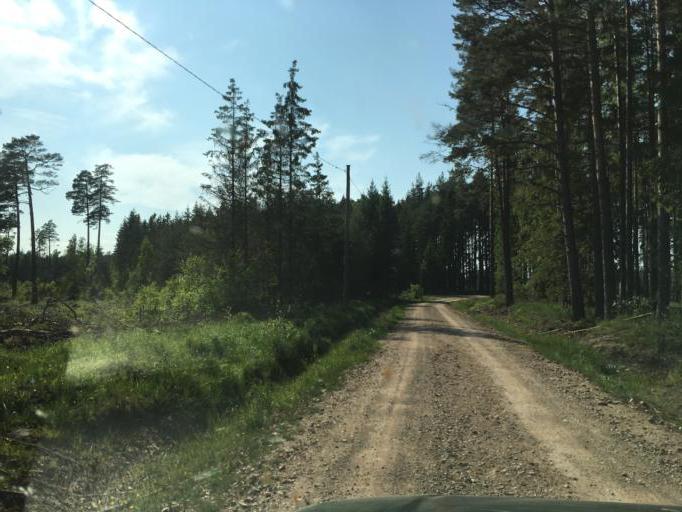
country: LV
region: Dundaga
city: Dundaga
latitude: 57.6120
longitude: 22.5056
